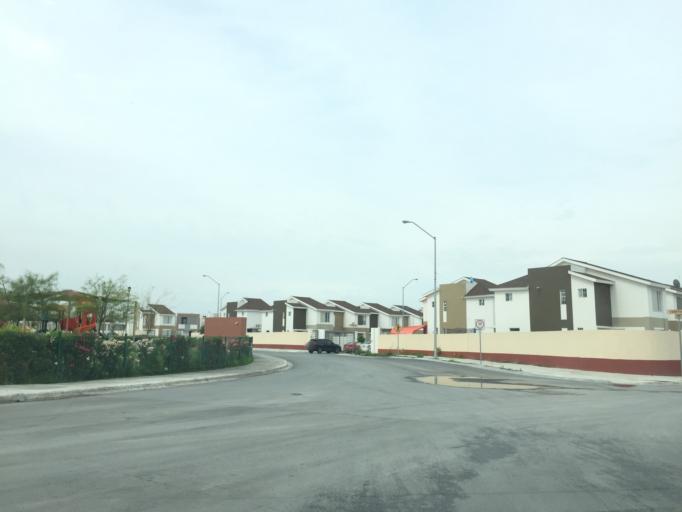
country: MX
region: Nuevo Leon
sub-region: Apodaca
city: Fraccionamiento Cosmopolis Octavo Sector
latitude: 25.8015
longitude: -100.2213
